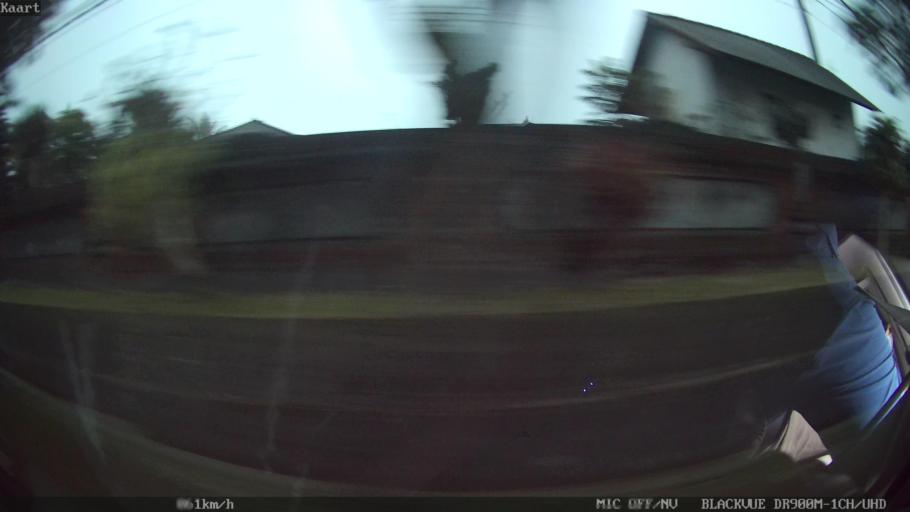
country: ID
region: Bali
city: Banjar Kedisan
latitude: -8.3051
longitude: 115.3070
